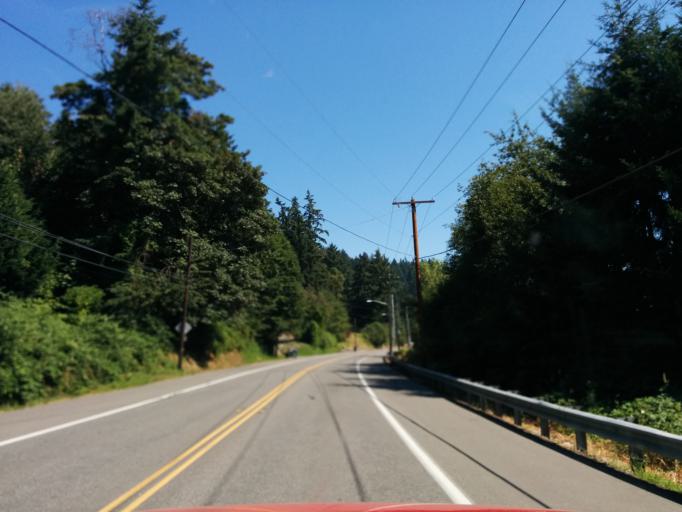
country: US
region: Washington
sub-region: King County
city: Sammamish
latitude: 47.6373
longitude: -122.0747
